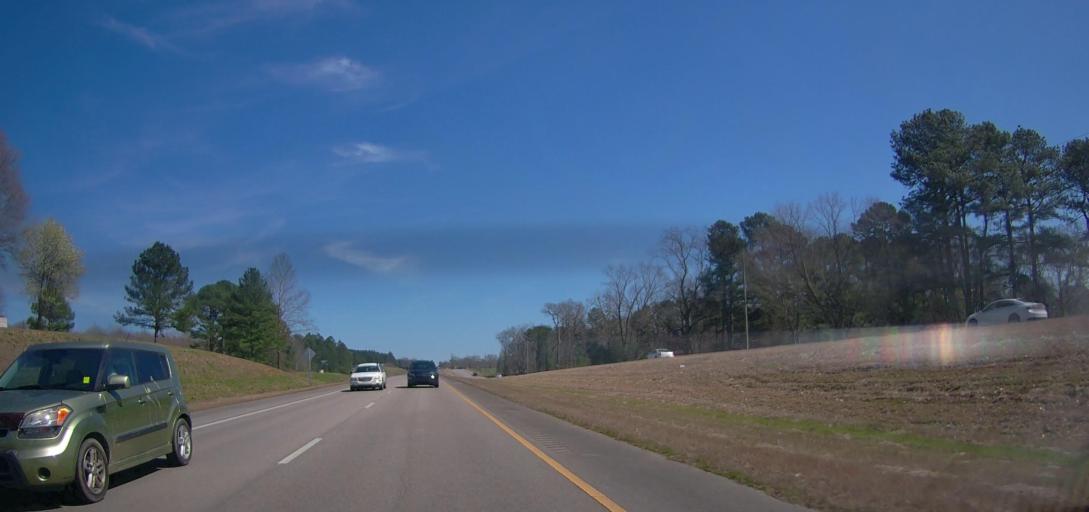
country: US
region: Alabama
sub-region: Cullman County
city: Cullman
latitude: 34.1765
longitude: -86.7242
